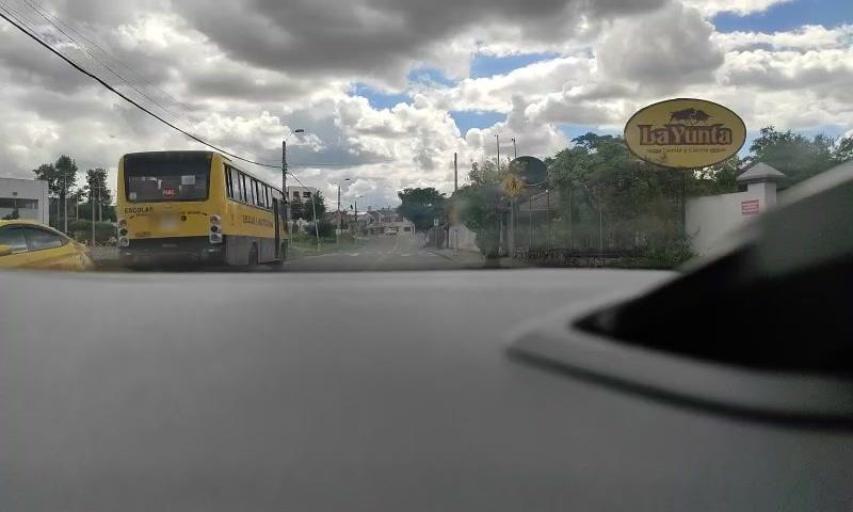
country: EC
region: Azuay
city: Cuenca
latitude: -2.9083
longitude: -79.0311
